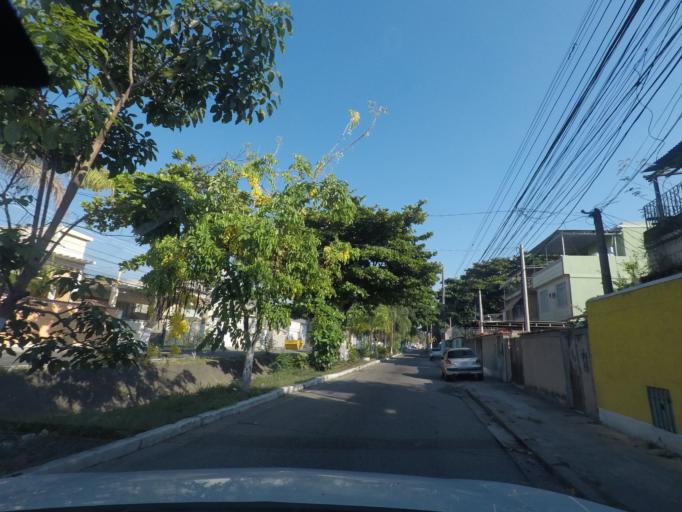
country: BR
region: Rio de Janeiro
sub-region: Duque De Caxias
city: Duque de Caxias
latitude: -22.8281
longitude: -43.2881
